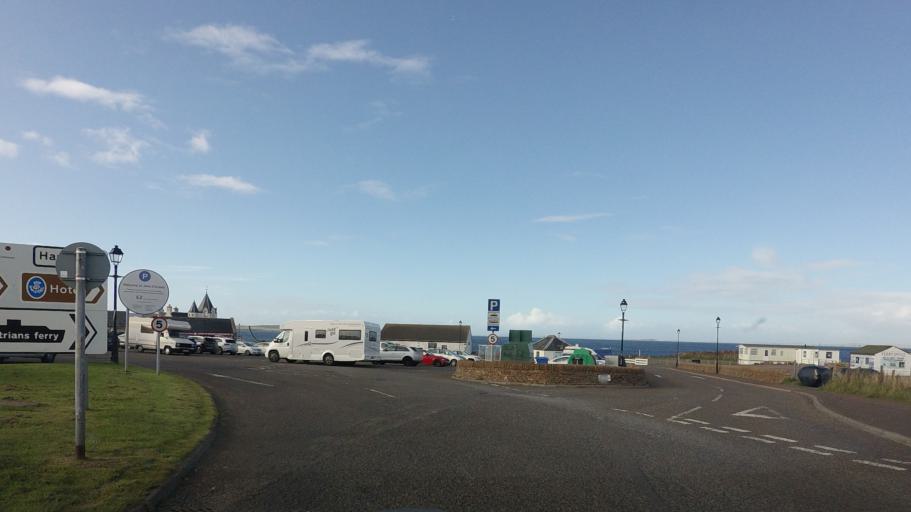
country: GB
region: Scotland
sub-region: Highland
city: Wick
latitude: 58.6427
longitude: -3.0687
